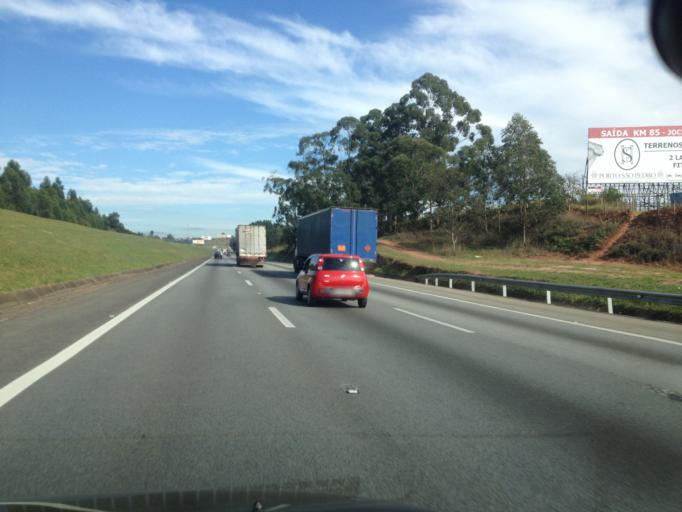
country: BR
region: Sao Paulo
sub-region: Mairinque
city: Mairinque
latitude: -23.4201
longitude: -47.2257
